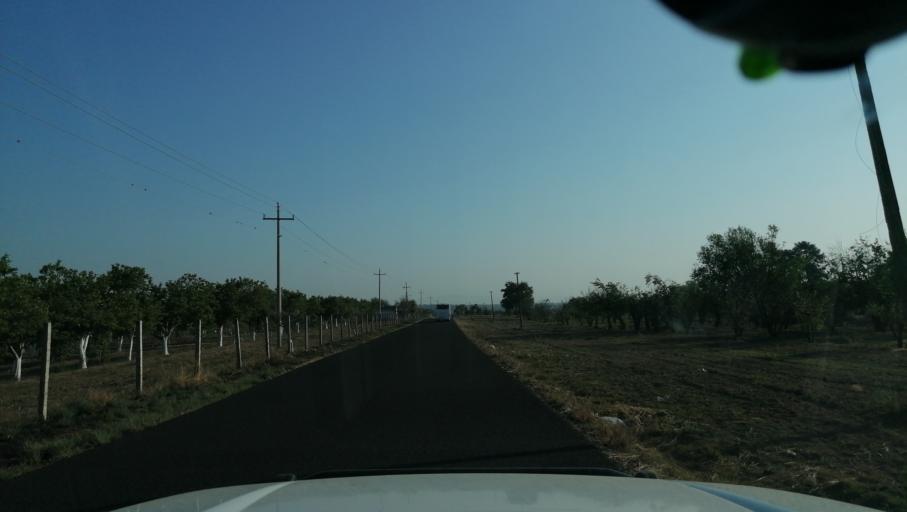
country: MX
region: Puebla
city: San Andres Calpan
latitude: 19.1095
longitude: -98.4223
